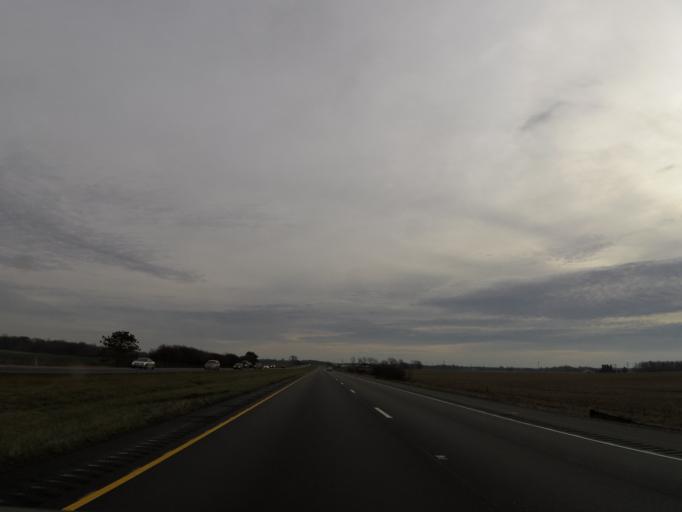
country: US
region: Indiana
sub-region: Montgomery County
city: Crawfordsville
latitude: 40.0924
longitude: -86.9644
